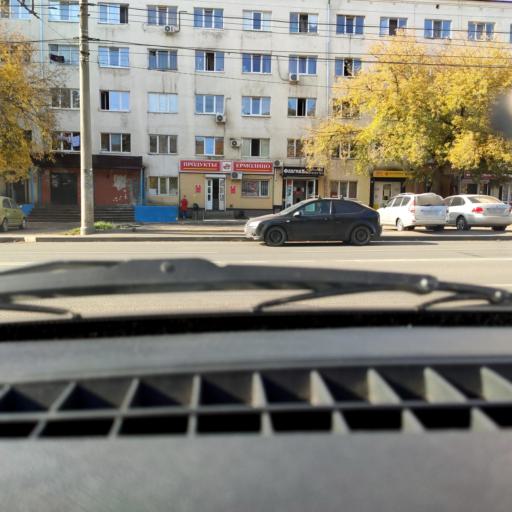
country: RU
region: Bashkortostan
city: Ufa
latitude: 54.8095
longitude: 56.1162
